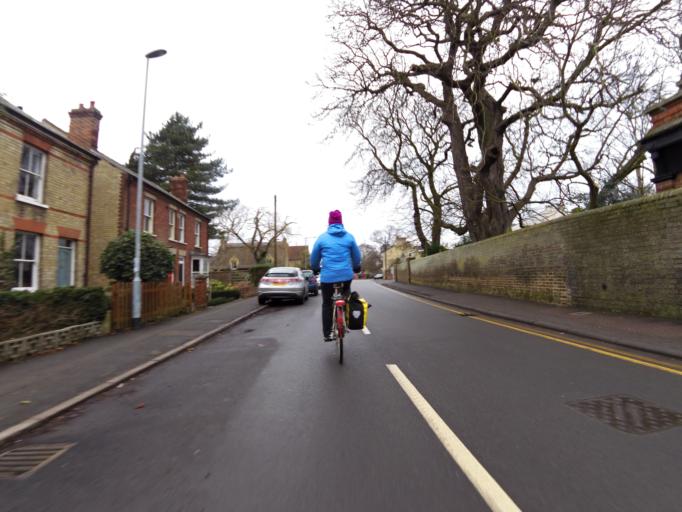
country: GB
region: England
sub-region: Cambridgeshire
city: Waterbeach
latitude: 52.2643
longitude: 0.1921
